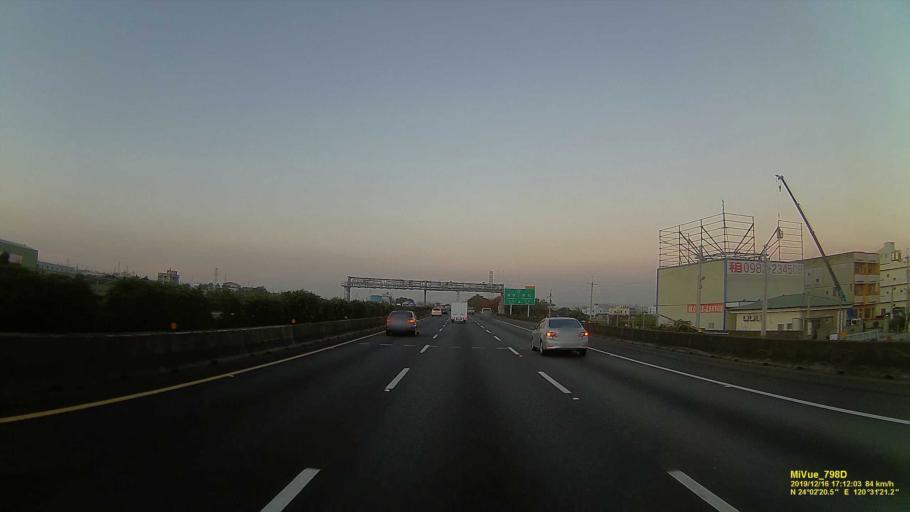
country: TW
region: Taiwan
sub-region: Changhua
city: Chang-hua
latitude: 24.0372
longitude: 120.5218
